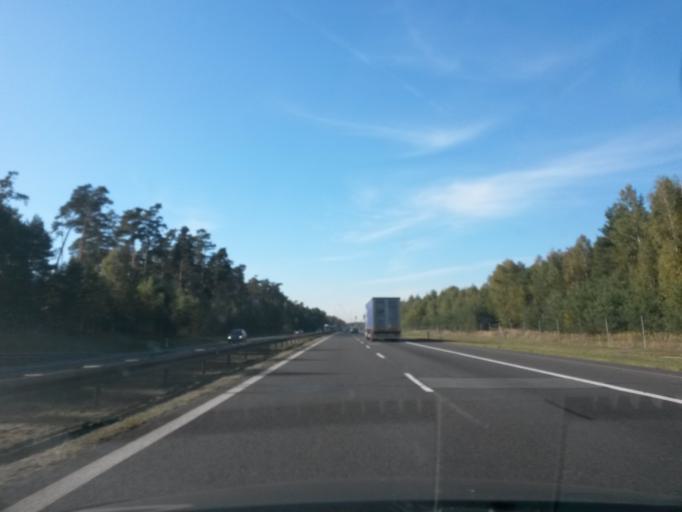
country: PL
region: Opole Voivodeship
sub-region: Powiat opolski
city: Niemodlin
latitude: 50.6719
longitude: 17.6654
